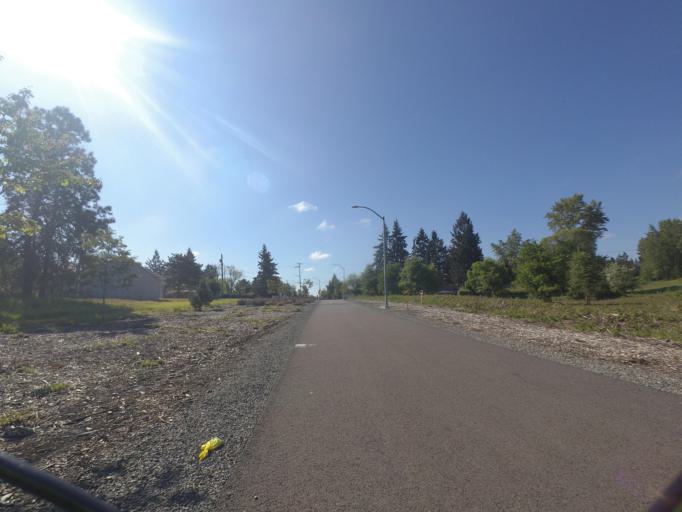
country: US
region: Washington
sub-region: Pierce County
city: Tacoma
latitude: 47.2180
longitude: -122.4145
